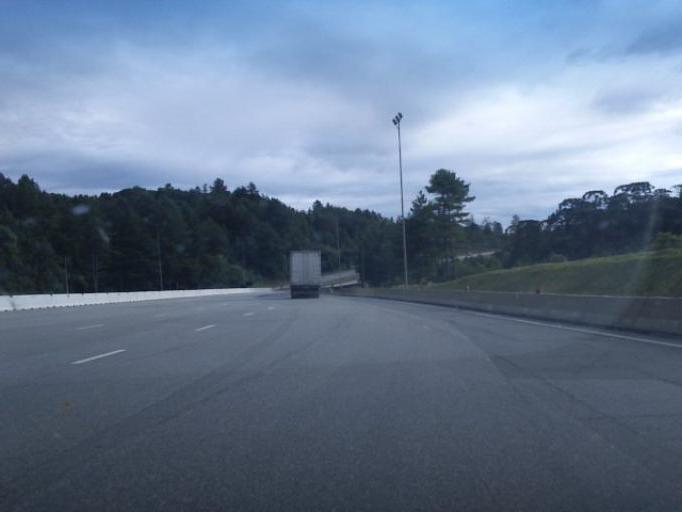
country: BR
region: Parana
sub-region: Campina Grande Do Sul
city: Campina Grande do Sul
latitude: -25.2904
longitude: -48.9345
